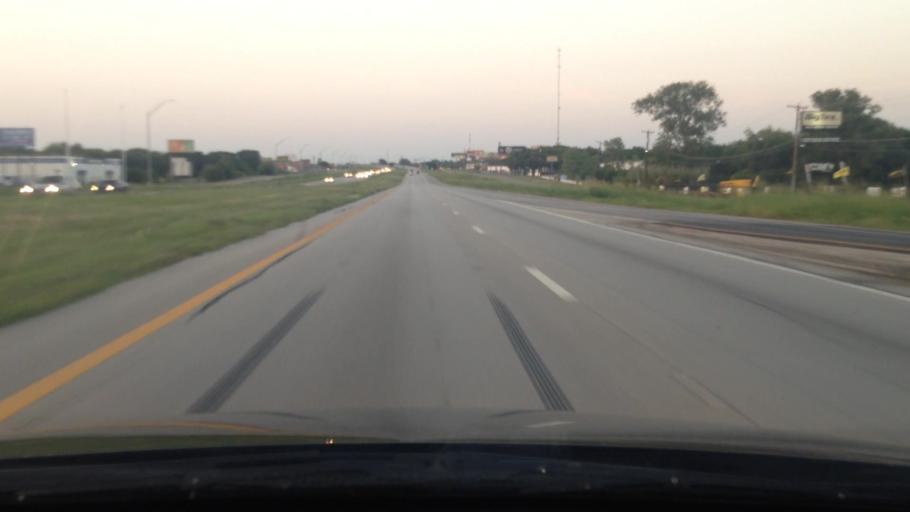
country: US
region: Texas
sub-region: Tarrant County
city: Forest Hill
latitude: 32.7101
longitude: -97.2302
